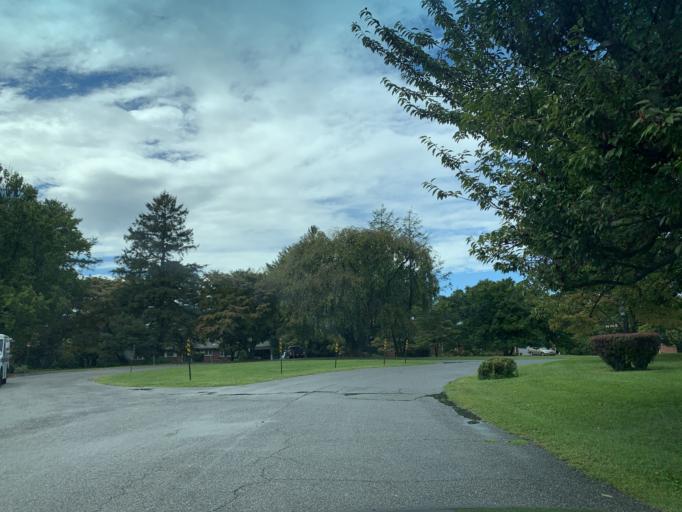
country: US
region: Maryland
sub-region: Baltimore County
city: Timonium
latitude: 39.4481
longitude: -76.6260
